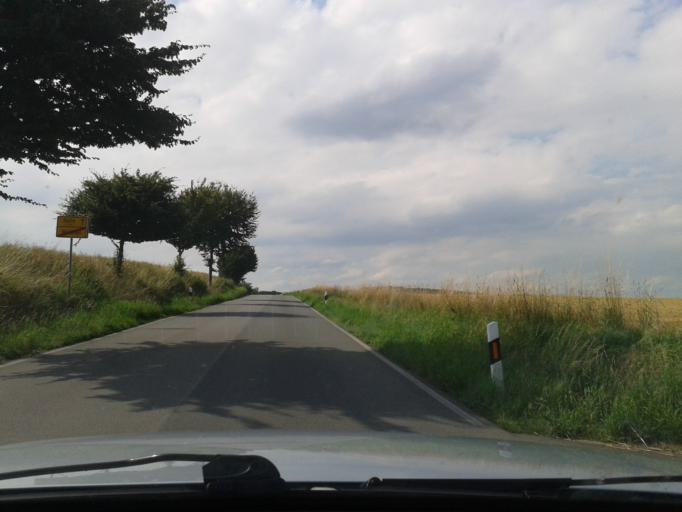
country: DE
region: North Rhine-Westphalia
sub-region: Regierungsbezirk Detmold
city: Steinheim
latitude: 51.8929
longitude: 9.0929
